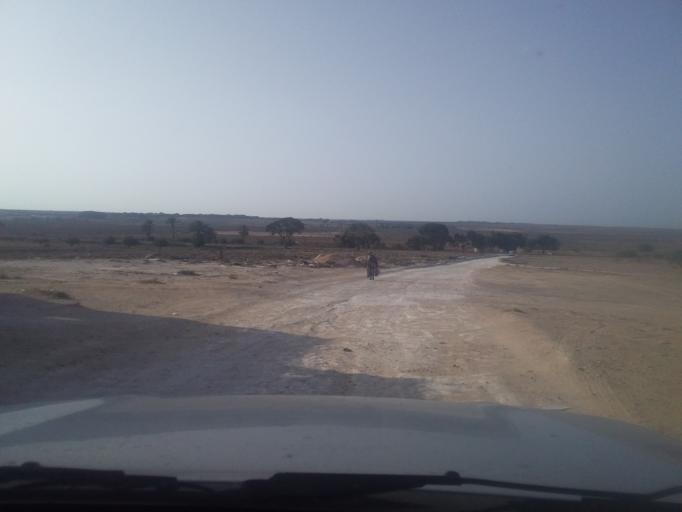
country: TN
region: Qabis
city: Gabes
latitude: 33.6391
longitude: 10.2928
